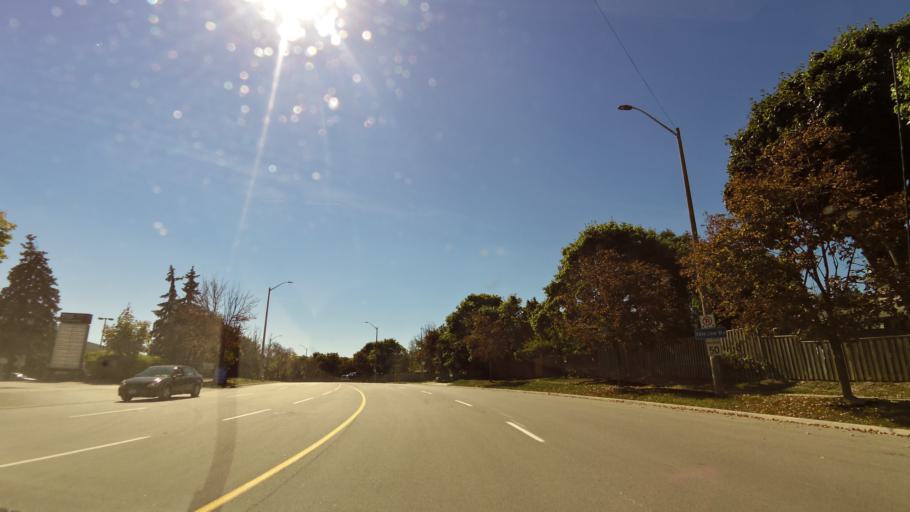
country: CA
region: Ontario
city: Mississauga
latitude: 43.5267
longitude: -79.6531
